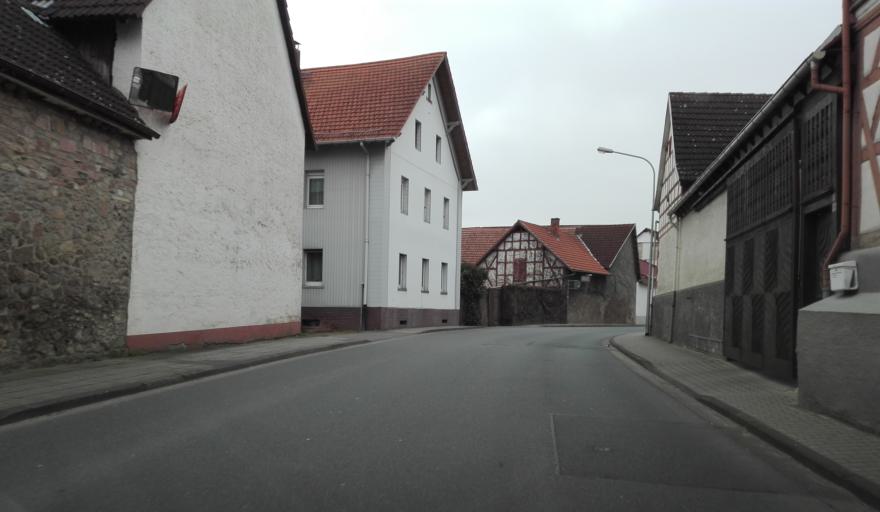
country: DE
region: Hesse
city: Ober-Ramstadt
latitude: 49.7877
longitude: 8.7406
